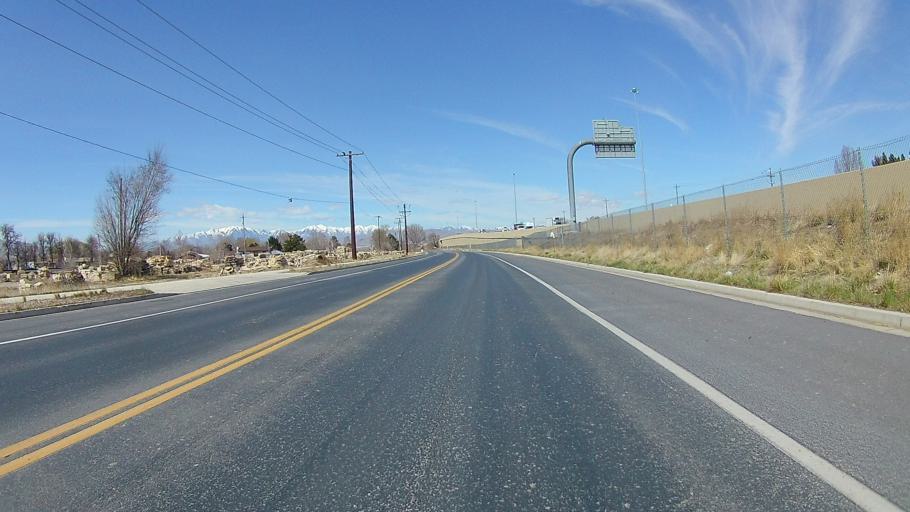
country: US
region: Utah
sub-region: Utah County
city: American Fork
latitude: 40.3713
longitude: -111.8034
